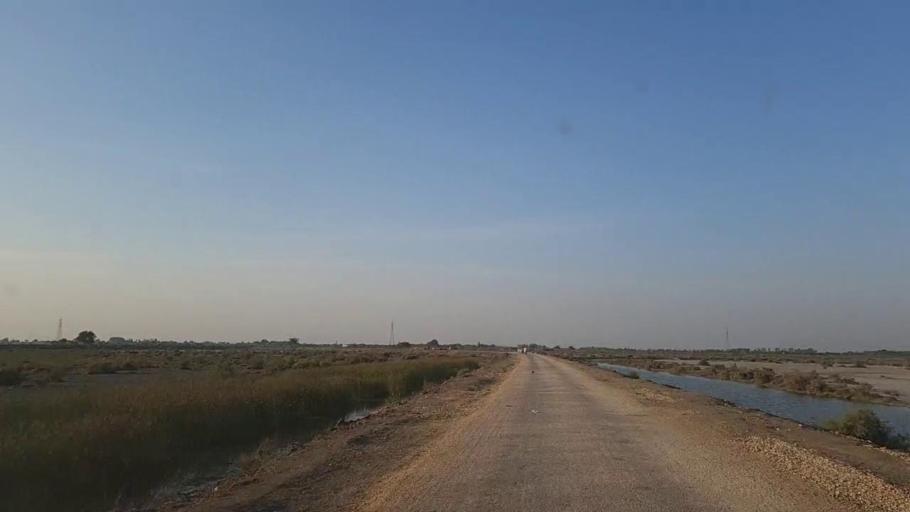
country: PK
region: Sindh
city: Mirpur Batoro
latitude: 24.6885
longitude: 68.2033
